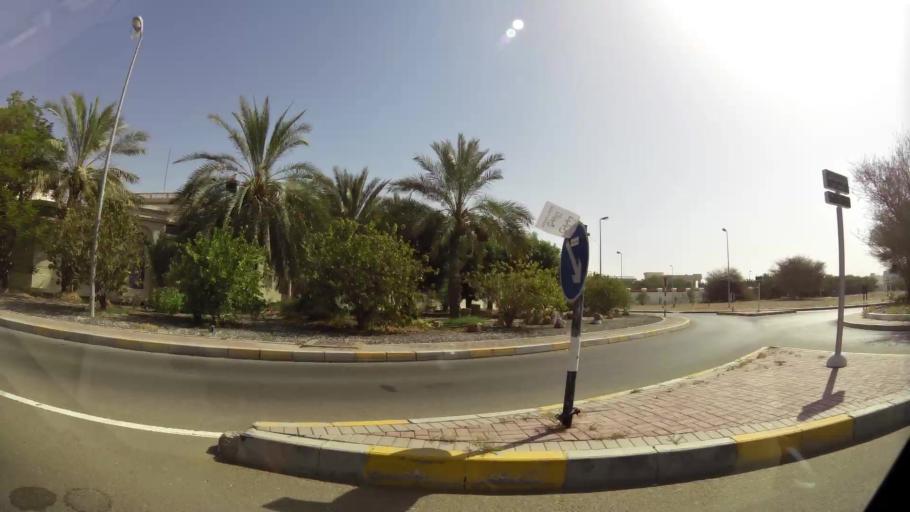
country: OM
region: Al Buraimi
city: Al Buraymi
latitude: 24.3138
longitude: 55.8020
